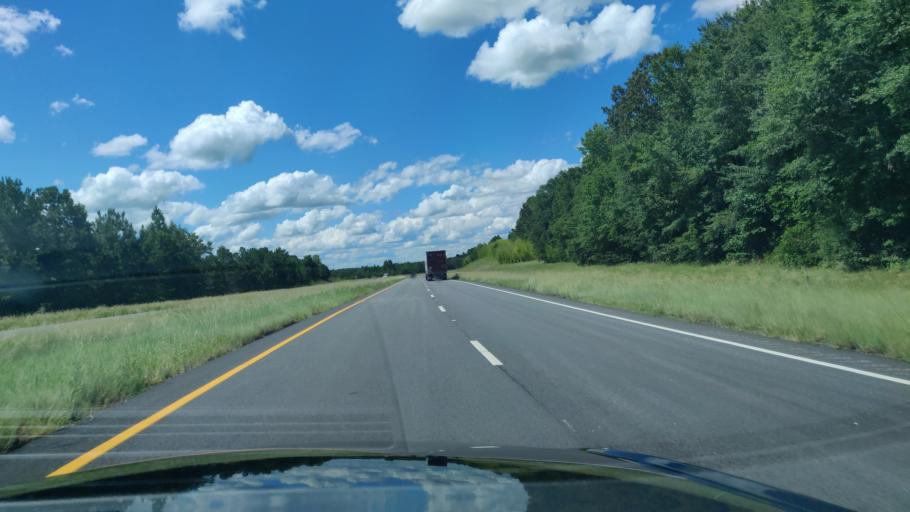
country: US
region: Georgia
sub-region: Stewart County
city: Richland
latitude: 32.1359
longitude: -84.6869
